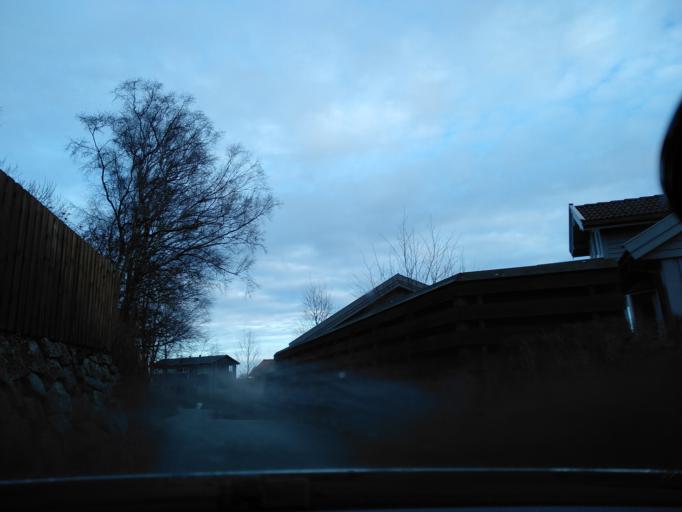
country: NO
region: Rogaland
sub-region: Sola
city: Sola
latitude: 58.9404
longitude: 5.6470
